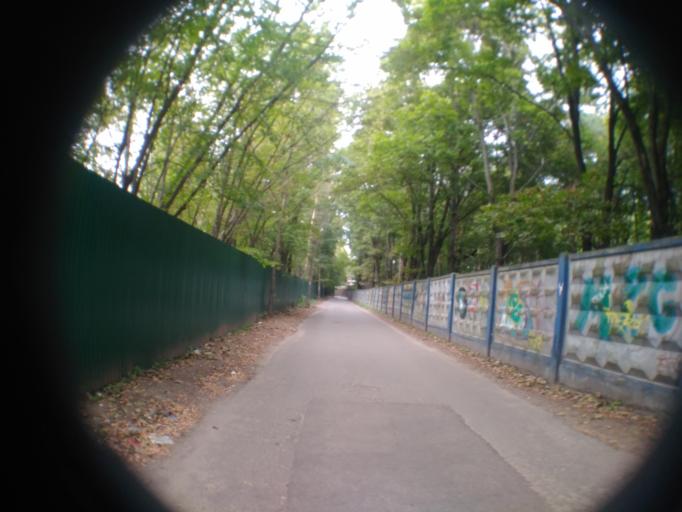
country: RU
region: Moskovskaya
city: Zhukovskiy
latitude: 55.5912
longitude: 38.1394
